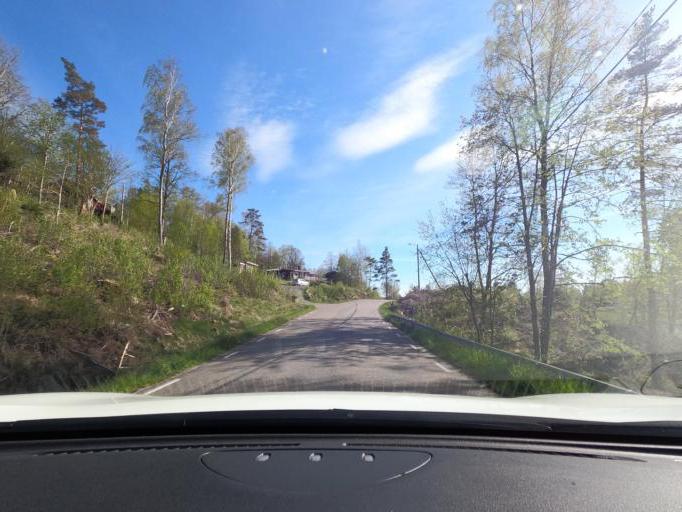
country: SE
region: Vaestra Goetaland
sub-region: Harryda Kommun
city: Hindas
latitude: 57.6440
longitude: 12.3523
